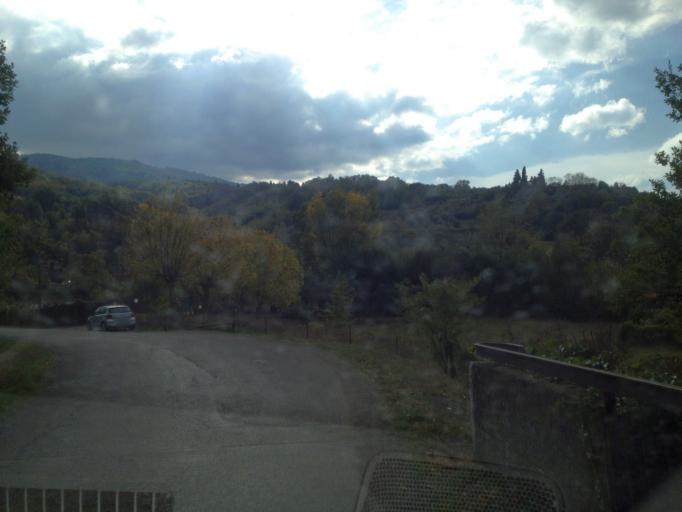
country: IT
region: Tuscany
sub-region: Province of Florence
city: Montebonello
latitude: 43.8513
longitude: 11.5031
